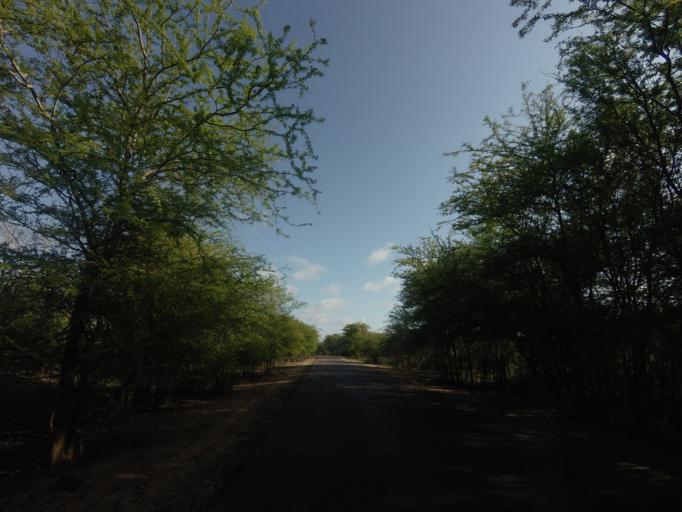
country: ZA
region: Mpumalanga
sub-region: Ehlanzeni District
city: Komatipoort
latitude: -25.2694
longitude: 31.8483
